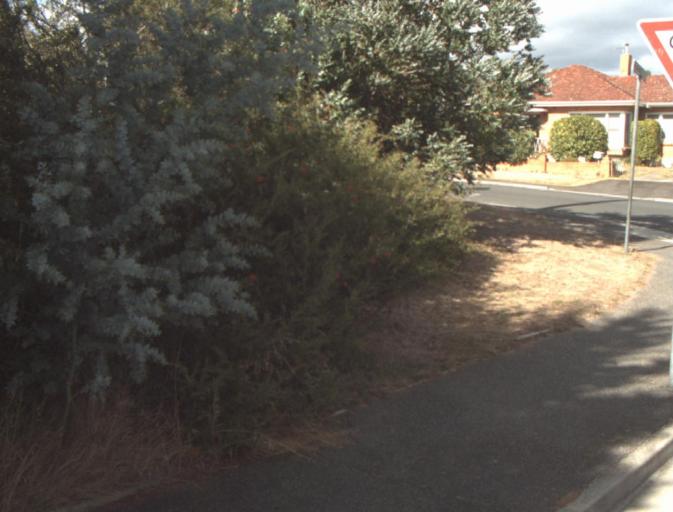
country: AU
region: Tasmania
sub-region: Launceston
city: Newstead
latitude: -41.4613
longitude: 147.1728
